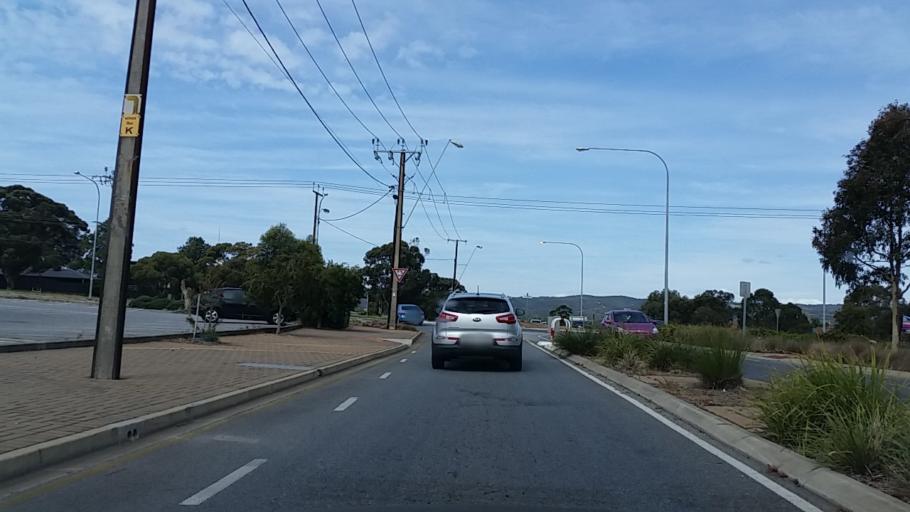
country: AU
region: South Australia
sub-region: Tea Tree Gully
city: Modbury
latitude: -34.8288
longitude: 138.6742
